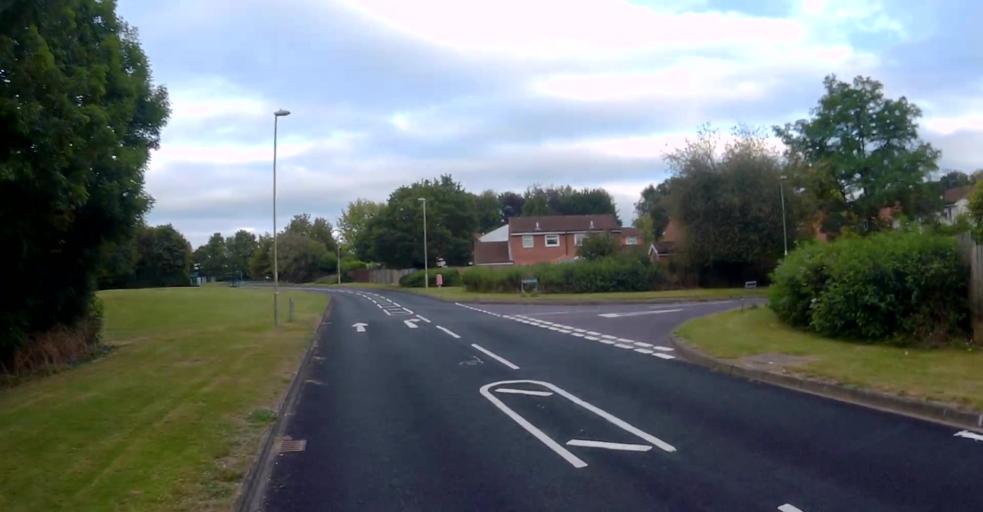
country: GB
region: England
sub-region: Hampshire
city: Basingstoke
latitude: 51.2380
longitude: -1.1179
